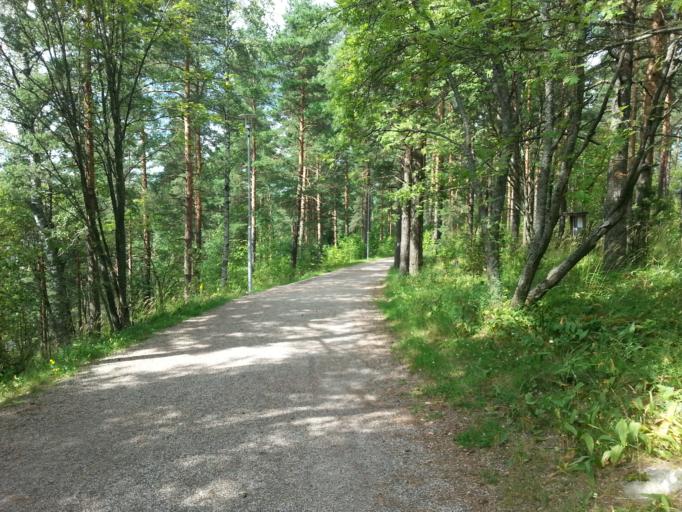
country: FI
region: Paijanne Tavastia
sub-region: Lahti
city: Lahti
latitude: 60.9791
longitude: 25.6435
